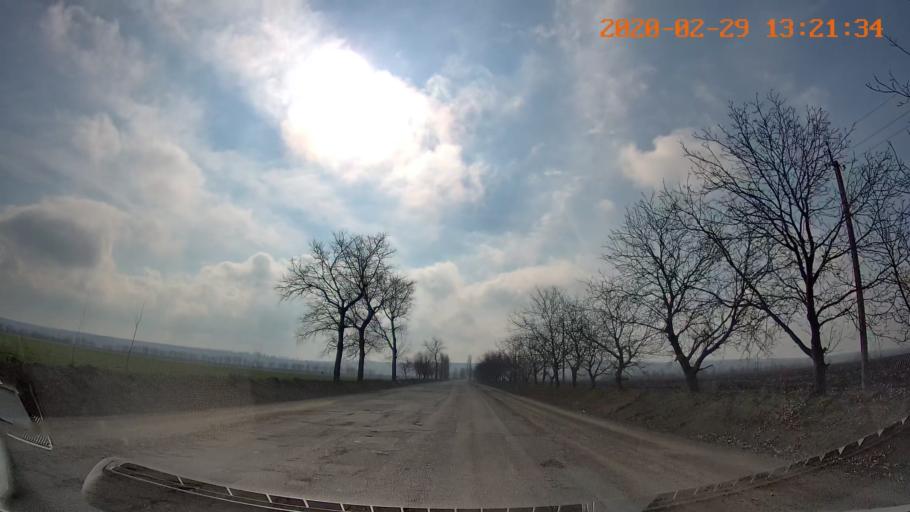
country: MD
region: Telenesti
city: Camenca
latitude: 47.9691
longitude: 28.6318
